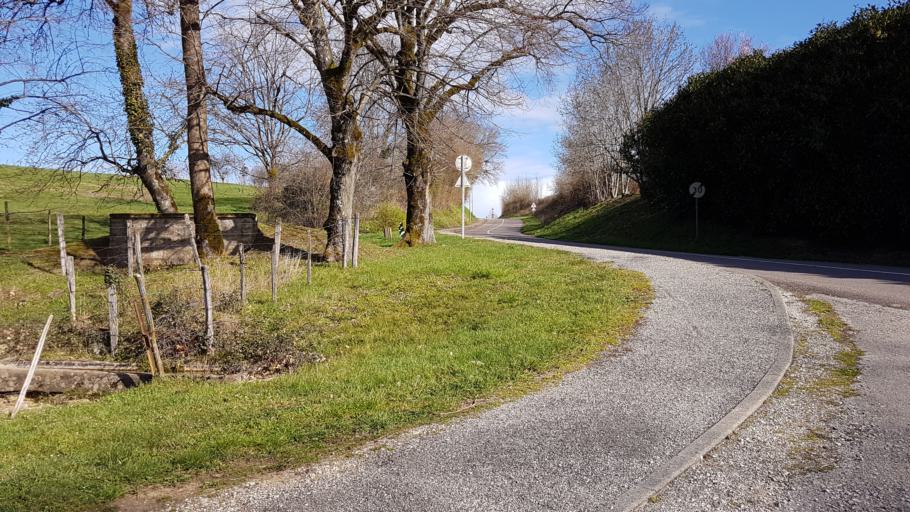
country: FR
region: Franche-Comte
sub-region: Departement du Jura
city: Lons-le-Saunier
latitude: 46.6932
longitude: 5.5508
